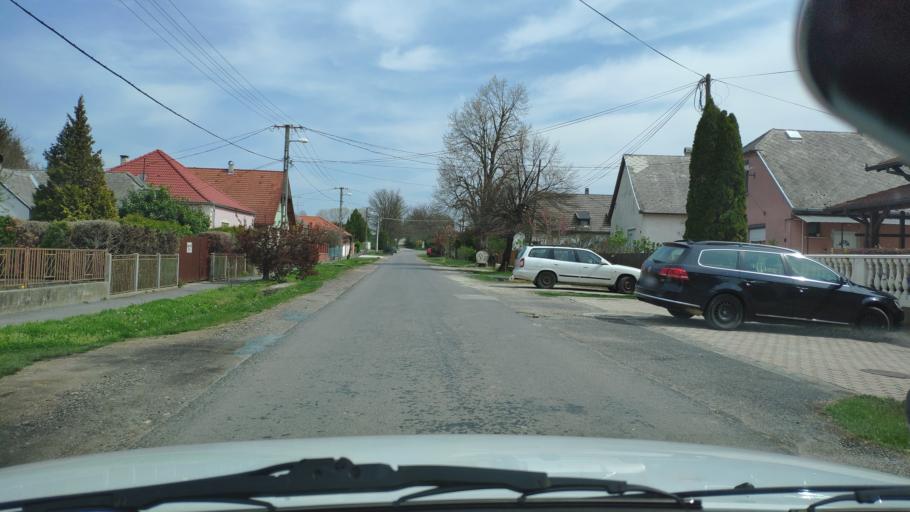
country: HU
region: Zala
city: Nagykanizsa
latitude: 46.4181
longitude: 16.9953
